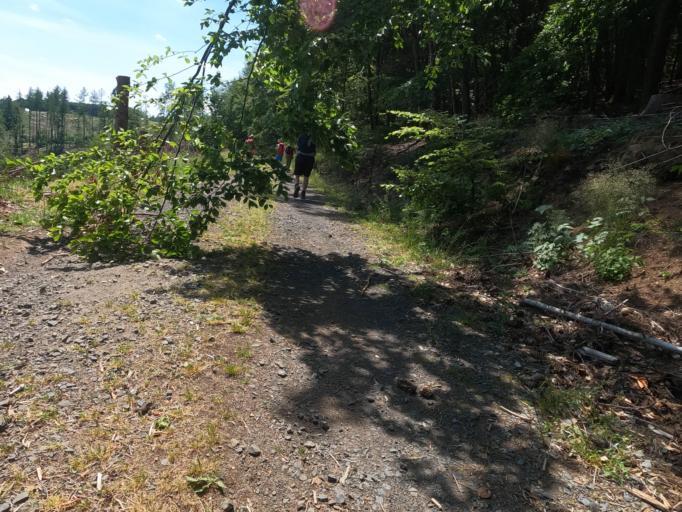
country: DE
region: Rheinland-Pfalz
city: Alpenrod
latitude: 50.6542
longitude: 7.8659
